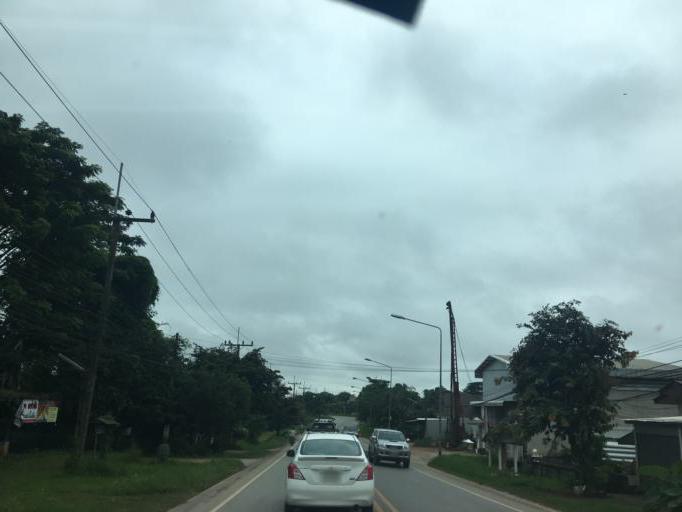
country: TH
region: Chiang Rai
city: Chiang Rai
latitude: 20.0043
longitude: 99.8766
